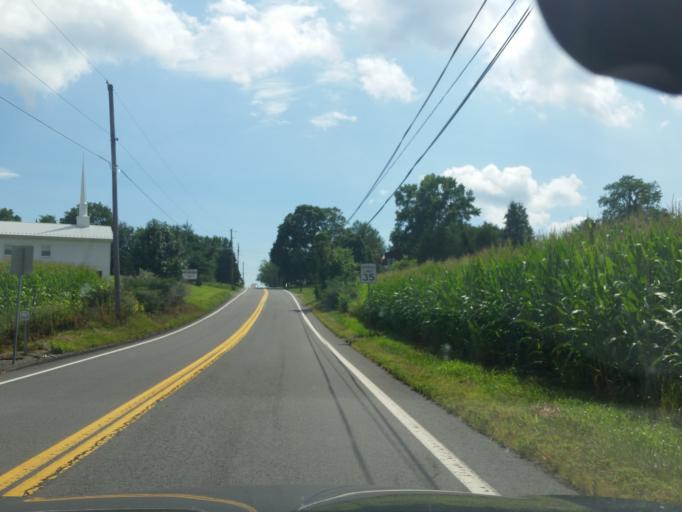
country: US
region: Pennsylvania
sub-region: Dauphin County
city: Elizabethville
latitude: 40.5079
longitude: -76.8789
